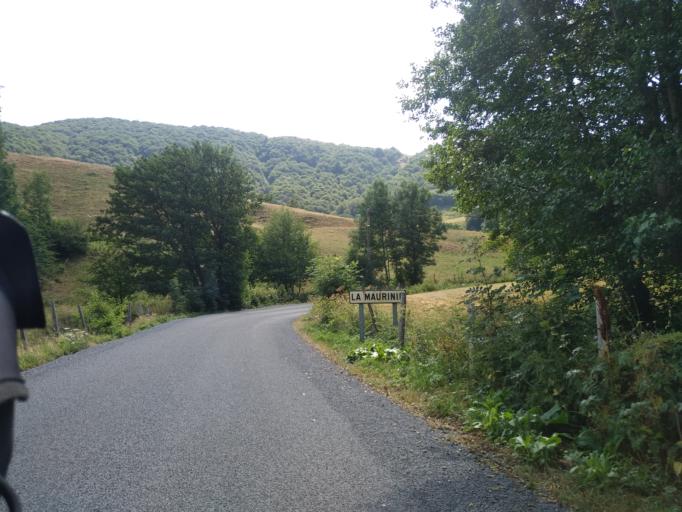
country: FR
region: Auvergne
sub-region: Departement du Cantal
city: Riom-es-Montagnes
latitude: 45.1379
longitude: 2.6982
